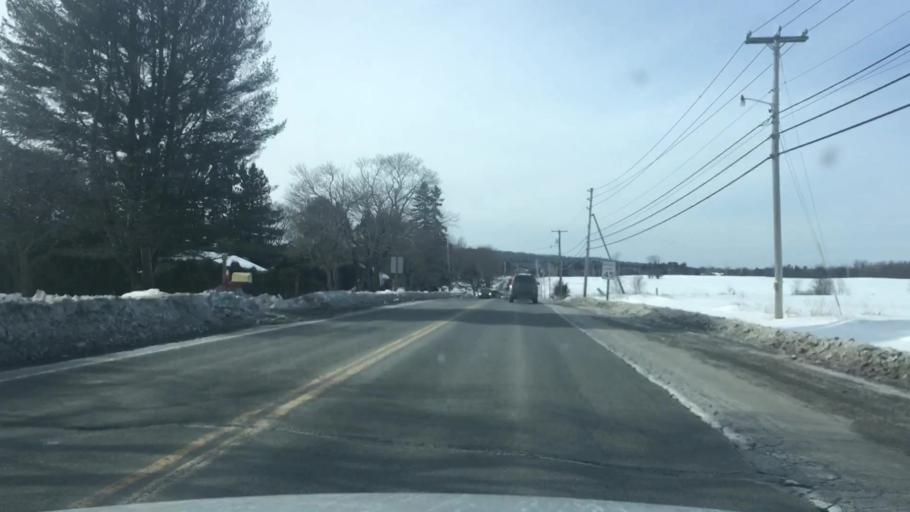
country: US
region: Maine
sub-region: Penobscot County
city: Bangor
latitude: 44.8536
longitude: -68.8127
